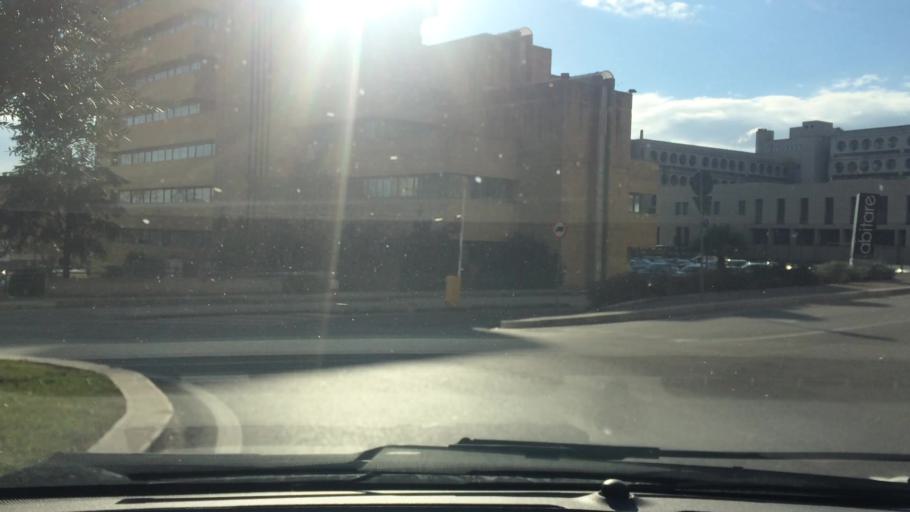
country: IT
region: Basilicate
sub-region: Provincia di Matera
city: Matera
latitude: 40.6674
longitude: 16.6001
